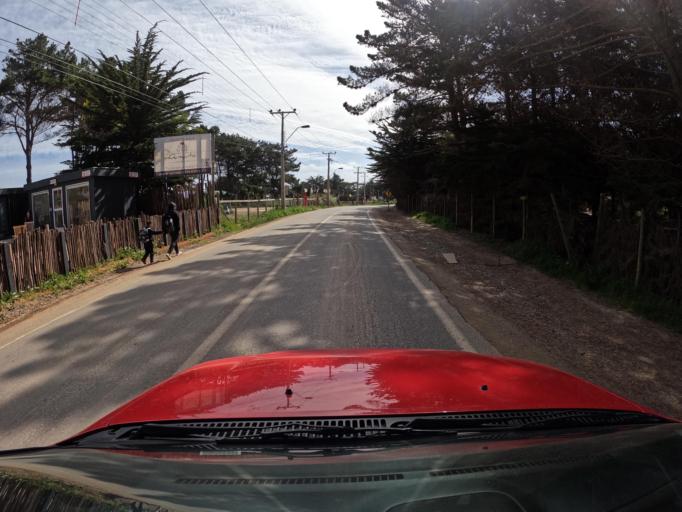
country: CL
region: O'Higgins
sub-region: Provincia de Colchagua
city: Santa Cruz
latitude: -34.4297
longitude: -72.0371
